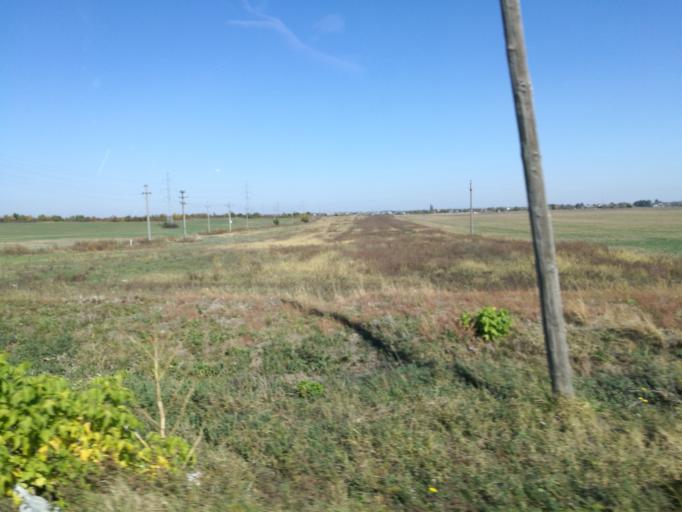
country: RO
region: Ilfov
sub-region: Comuna Dragomiresti-Vale
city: Dragomiresti-Vale
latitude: 44.4728
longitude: 25.9131
